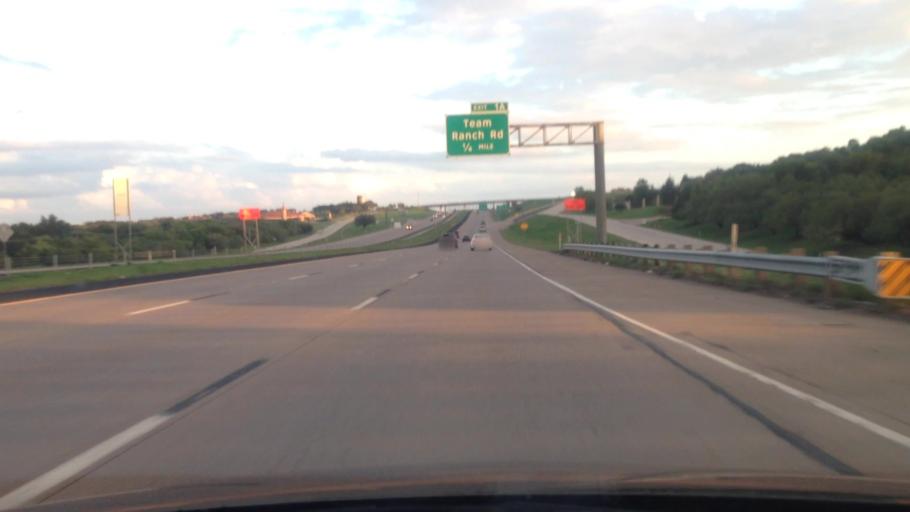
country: US
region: Texas
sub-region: Tarrant County
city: Benbrook
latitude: 32.7105
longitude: -97.4767
